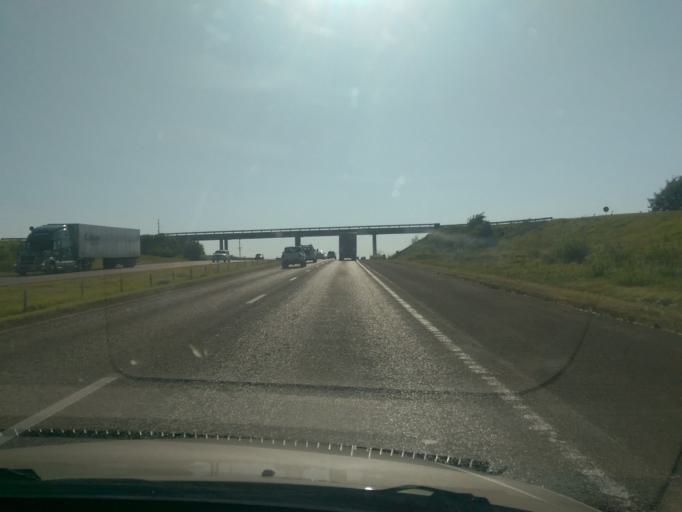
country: US
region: Missouri
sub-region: Lafayette County
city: Concordia
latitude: 38.9897
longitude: -93.6306
